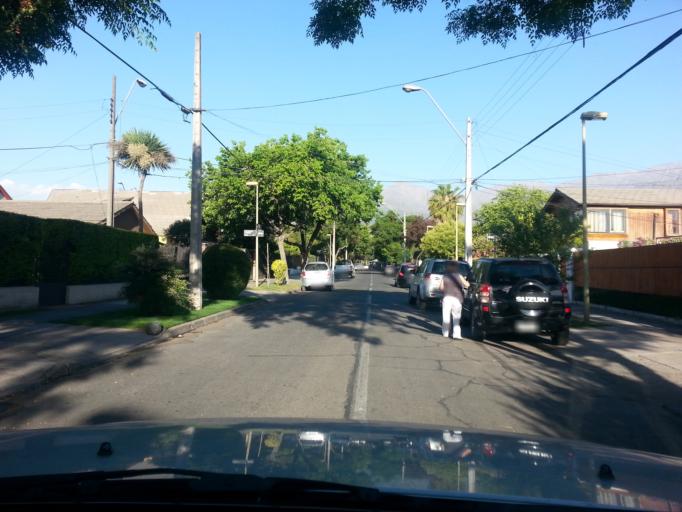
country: CL
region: Santiago Metropolitan
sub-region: Provincia de Santiago
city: Villa Presidente Frei, Nunoa, Santiago, Chile
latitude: -33.4288
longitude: -70.5735
